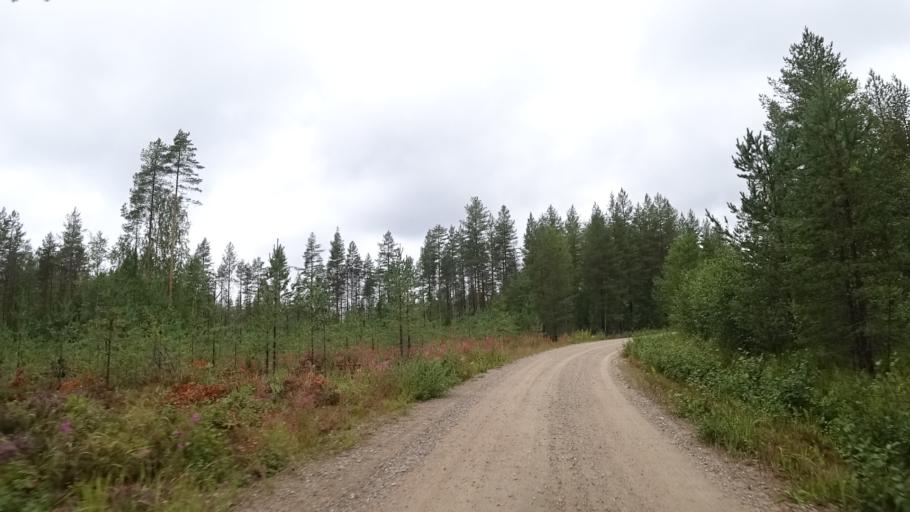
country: FI
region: North Karelia
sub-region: Pielisen Karjala
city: Lieksa
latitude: 63.5161
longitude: 30.1175
